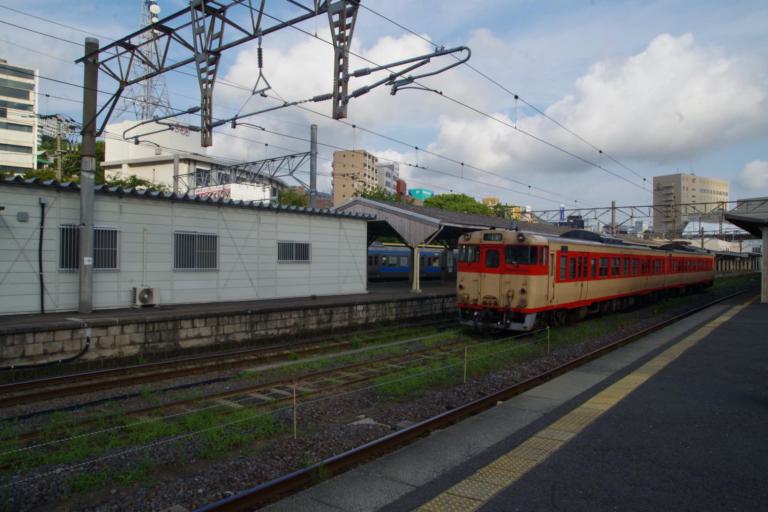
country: JP
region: Nagasaki
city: Nagasaki-shi
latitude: 32.7542
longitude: 129.8696
